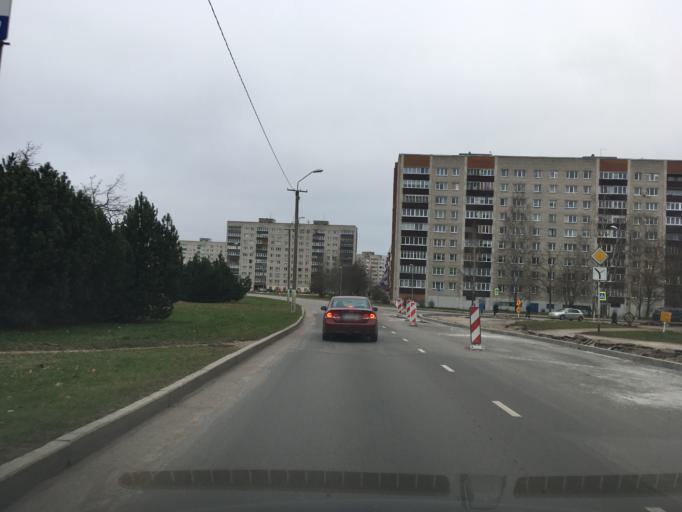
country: EE
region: Ida-Virumaa
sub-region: Narva linn
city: Narva
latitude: 59.3821
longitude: 28.1800
